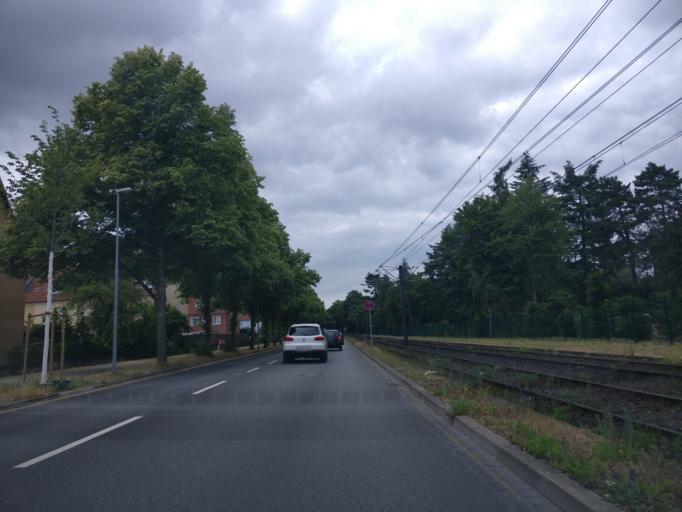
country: DE
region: Lower Saxony
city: Laatzen
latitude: 52.3352
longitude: 9.7892
